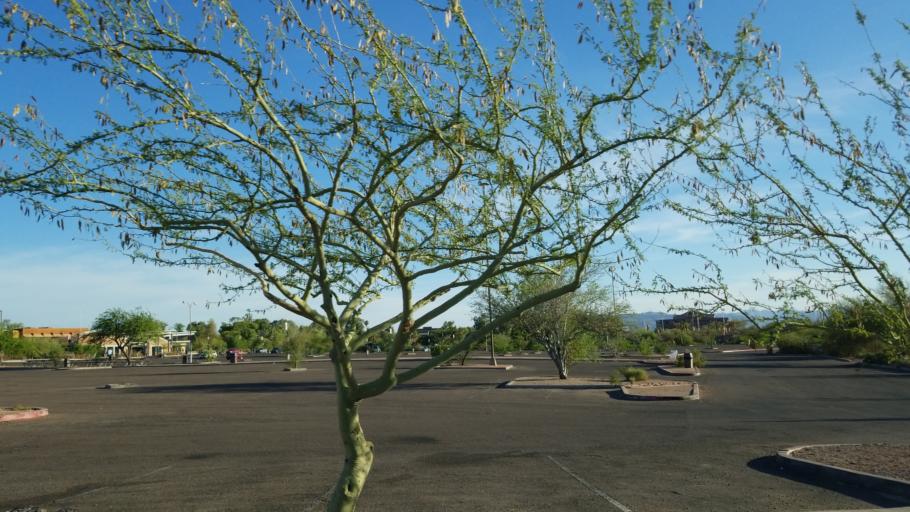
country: US
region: Arizona
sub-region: Maricopa County
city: Tempe Junction
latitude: 33.4539
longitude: -111.9491
